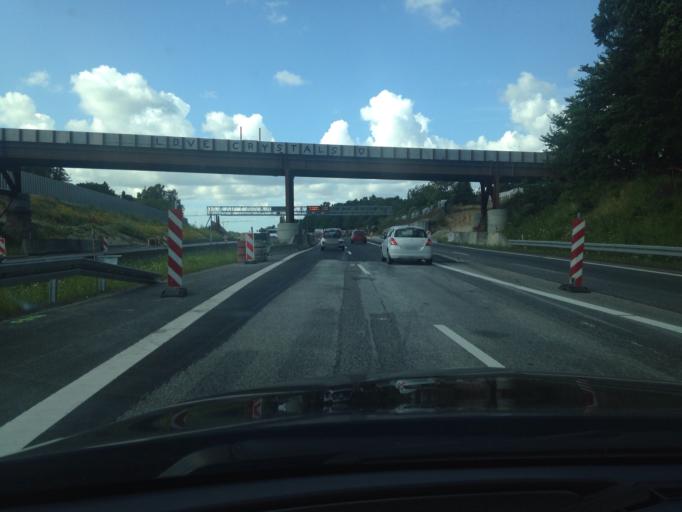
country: DK
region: Capital Region
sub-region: Rudersdal Kommune
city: Trorod
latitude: 55.8269
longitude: 12.5259
